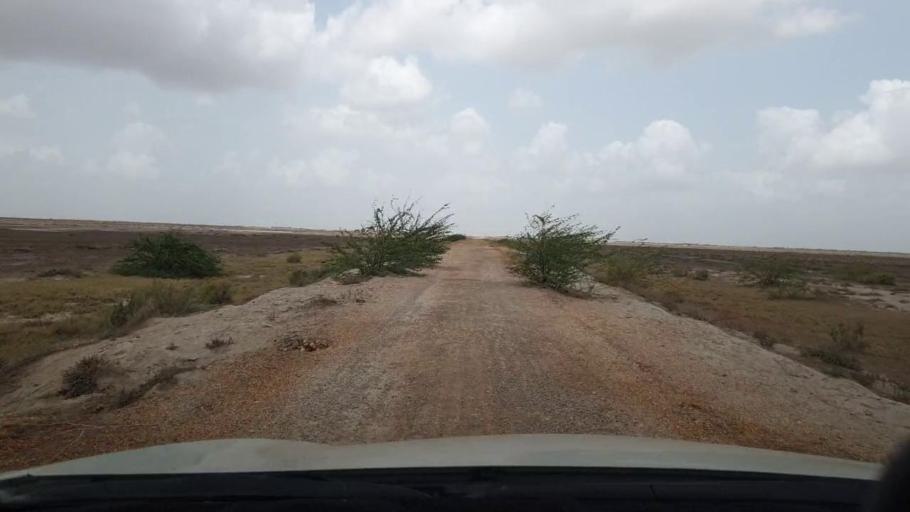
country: PK
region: Sindh
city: Kadhan
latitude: 24.3603
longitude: 68.8360
